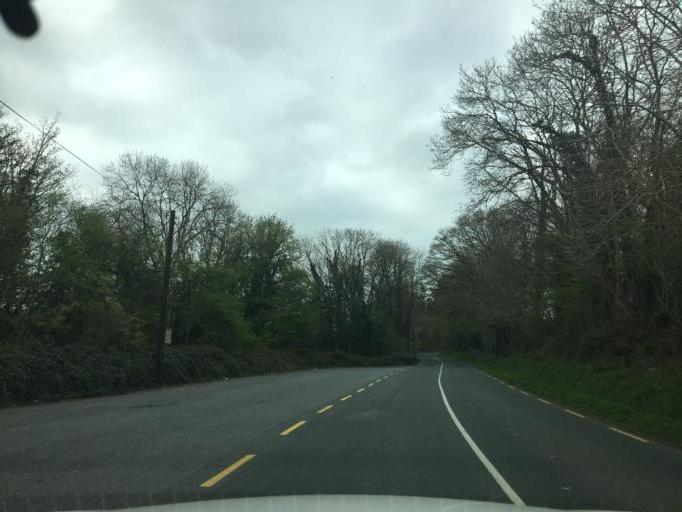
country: IE
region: Leinster
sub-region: Kilkenny
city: Graiguenamanagh
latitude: 52.4693
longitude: -7.0016
